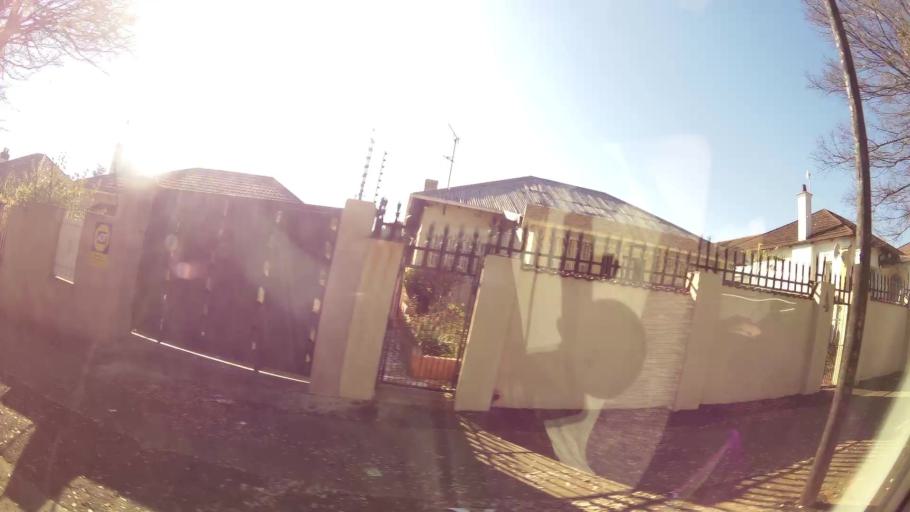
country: ZA
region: Gauteng
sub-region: City of Johannesburg Metropolitan Municipality
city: Johannesburg
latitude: -26.1981
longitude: 28.0960
